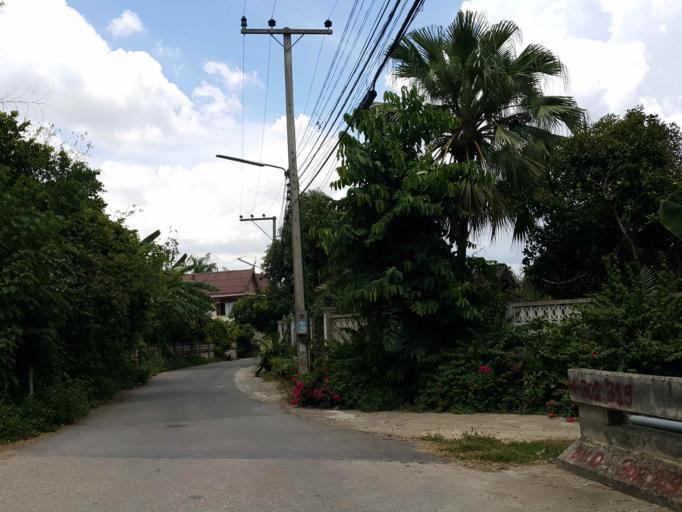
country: TH
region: Chiang Mai
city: Chiang Mai
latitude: 18.7486
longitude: 98.9907
